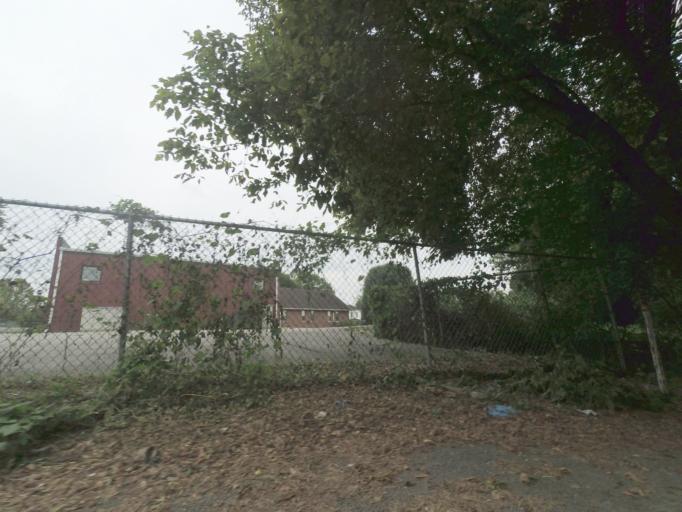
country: US
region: West Virginia
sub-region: Cabell County
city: Huntington
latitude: 38.4162
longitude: -82.4316
